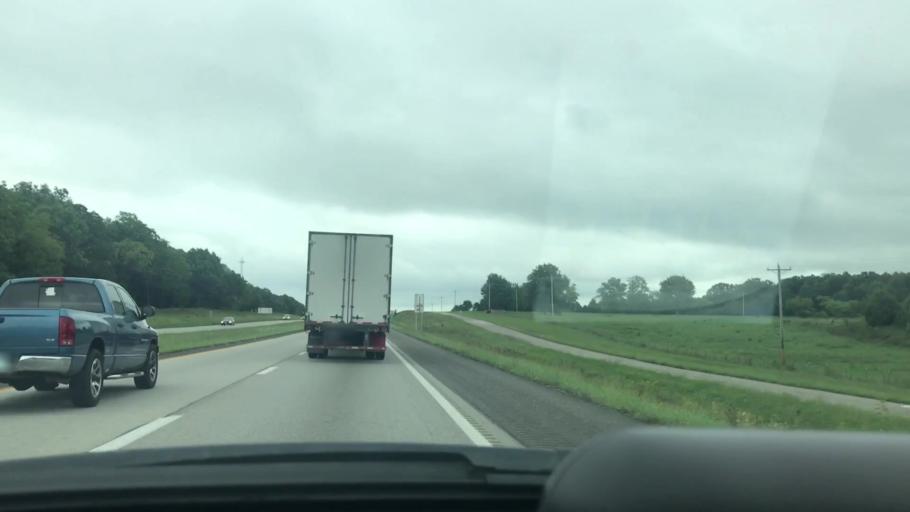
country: US
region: Missouri
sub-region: Greene County
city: Republic
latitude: 37.1858
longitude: -93.5601
